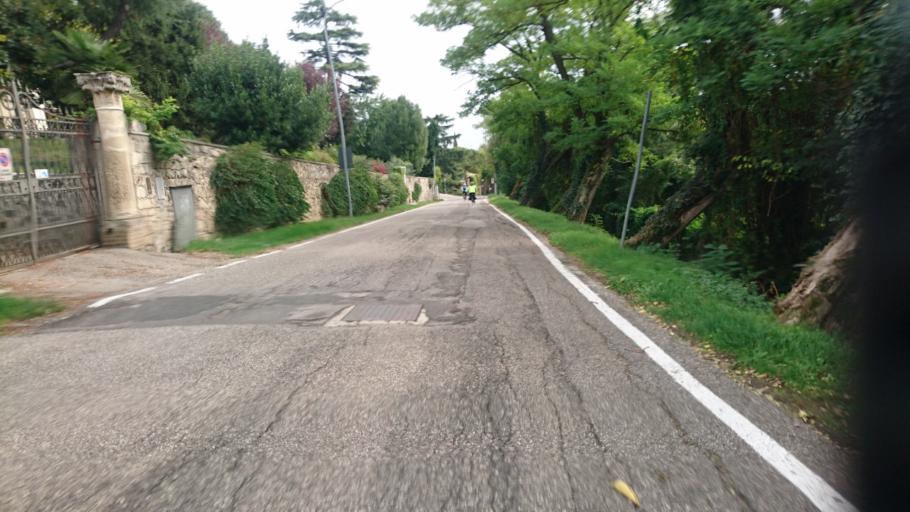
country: IT
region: Veneto
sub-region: Provincia di Verona
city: Caldiero
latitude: 45.4102
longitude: 11.1919
